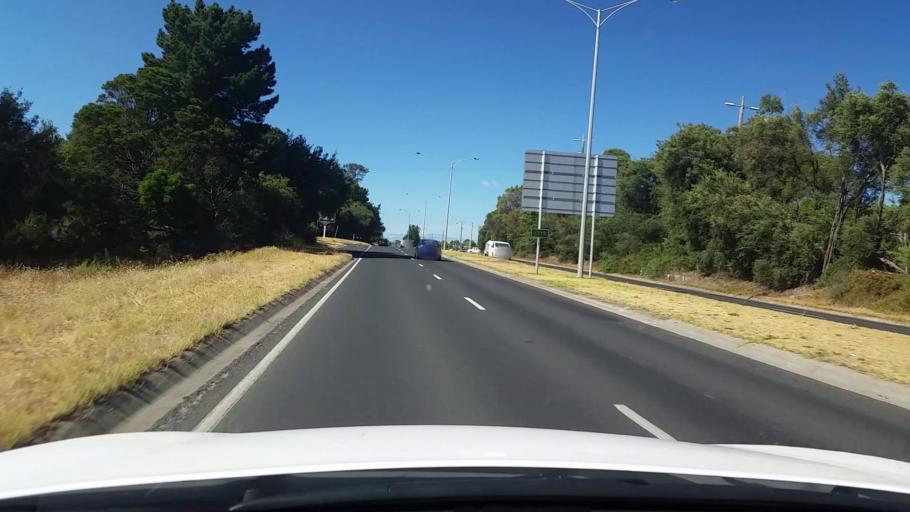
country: AU
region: Victoria
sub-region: Mornington Peninsula
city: Rosebud West
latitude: -38.3775
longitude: 144.8892
